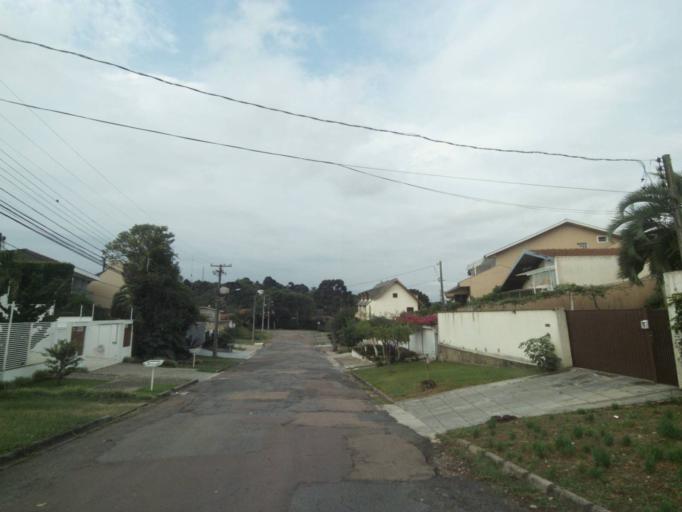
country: BR
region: Parana
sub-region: Curitiba
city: Curitiba
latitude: -25.4006
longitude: -49.2793
